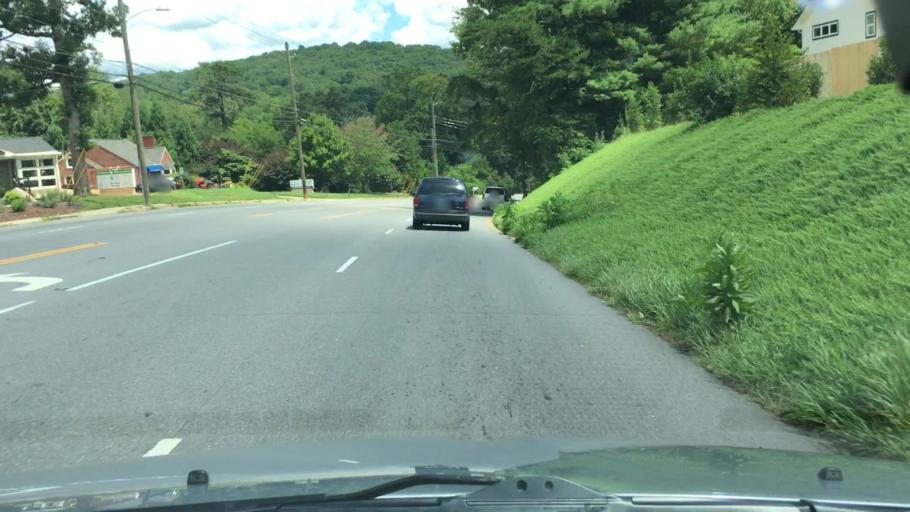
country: US
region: North Carolina
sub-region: Buncombe County
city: Asheville
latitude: 35.5893
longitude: -82.4996
